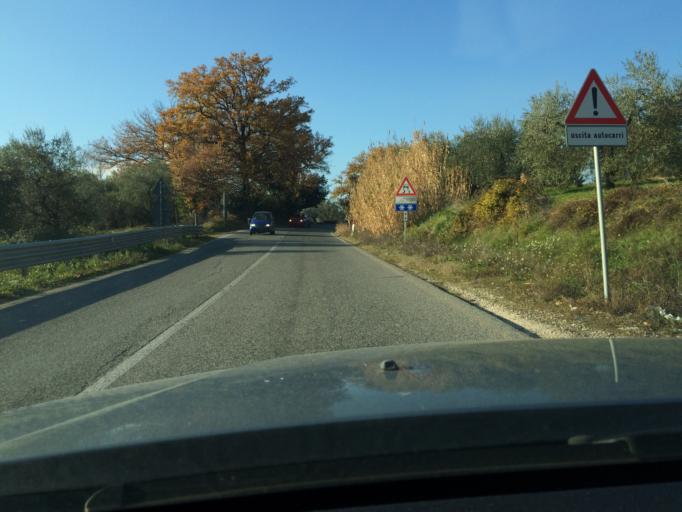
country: IT
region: Umbria
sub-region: Provincia di Terni
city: Fornole
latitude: 42.5521
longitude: 12.4431
